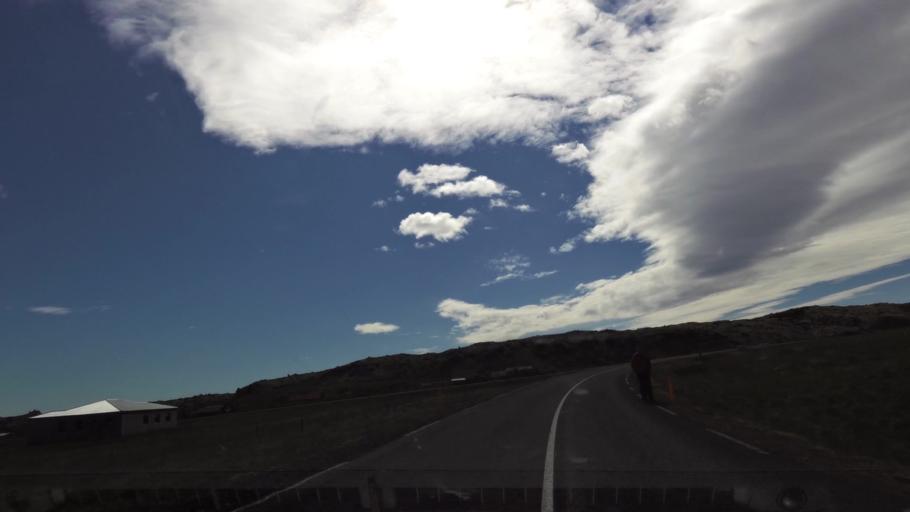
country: IS
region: West
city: Olafsvik
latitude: 64.7684
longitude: -23.6427
